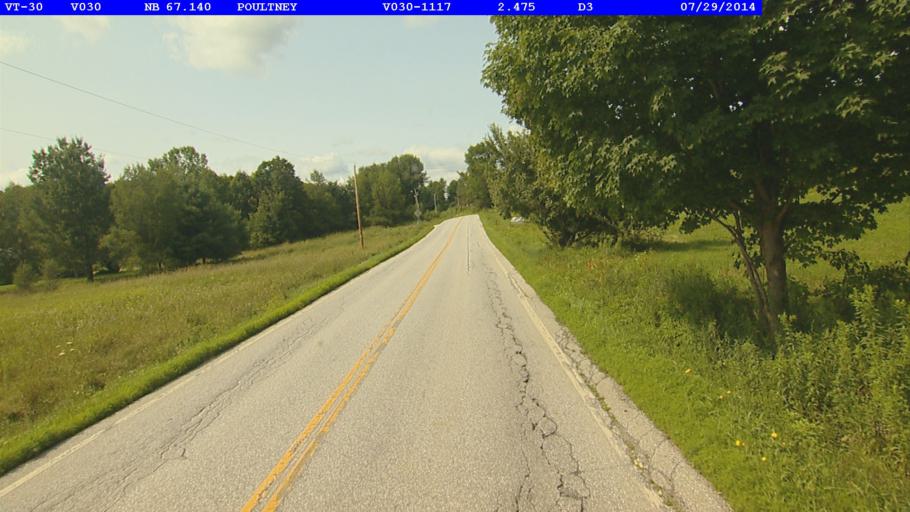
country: US
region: Vermont
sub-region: Rutland County
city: Poultney
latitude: 43.4978
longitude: -73.2069
